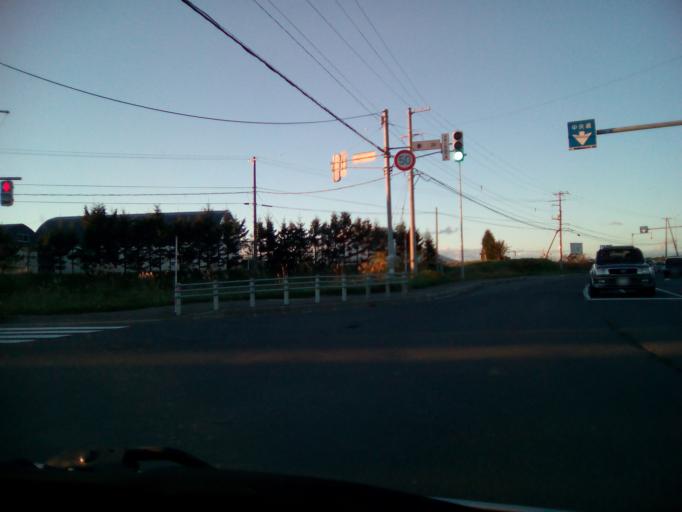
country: JP
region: Hokkaido
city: Niseko Town
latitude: 42.6626
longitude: 140.8121
